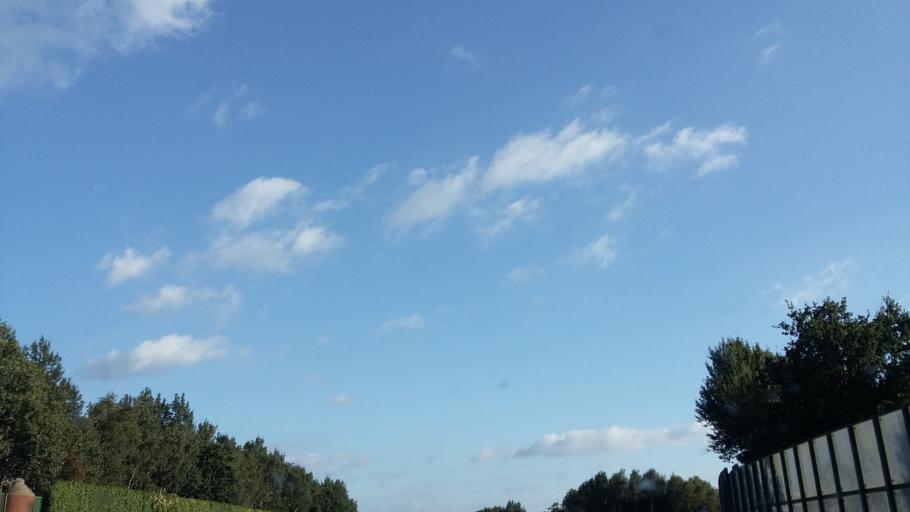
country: DE
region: Lower Saxony
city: Schiffdorf
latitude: 53.5294
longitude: 8.6226
